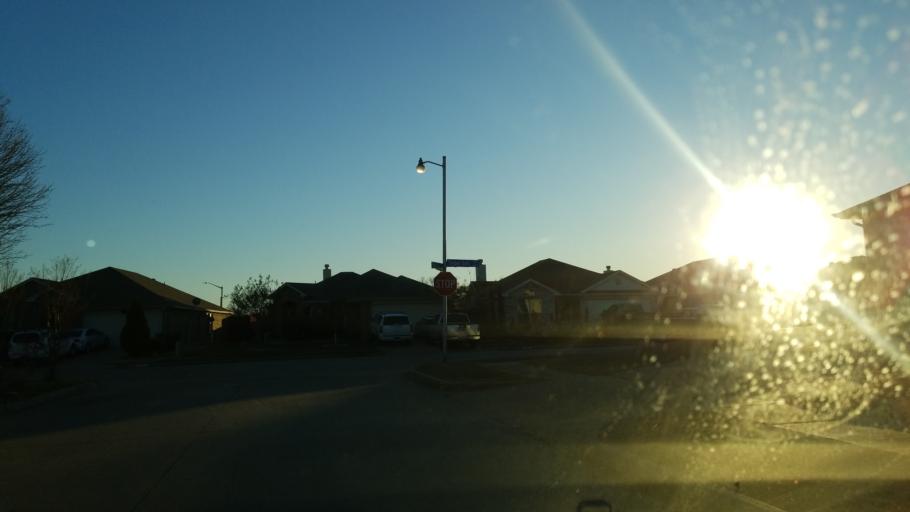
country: US
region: Texas
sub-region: Dallas County
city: Grand Prairie
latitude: 32.7261
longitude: -97.0506
